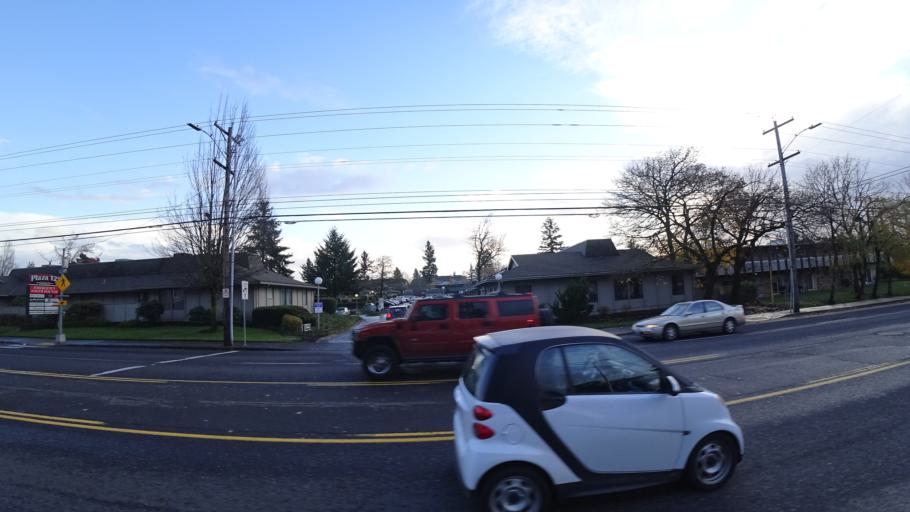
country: US
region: Oregon
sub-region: Multnomah County
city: Lents
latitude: 45.5191
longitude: -122.5338
